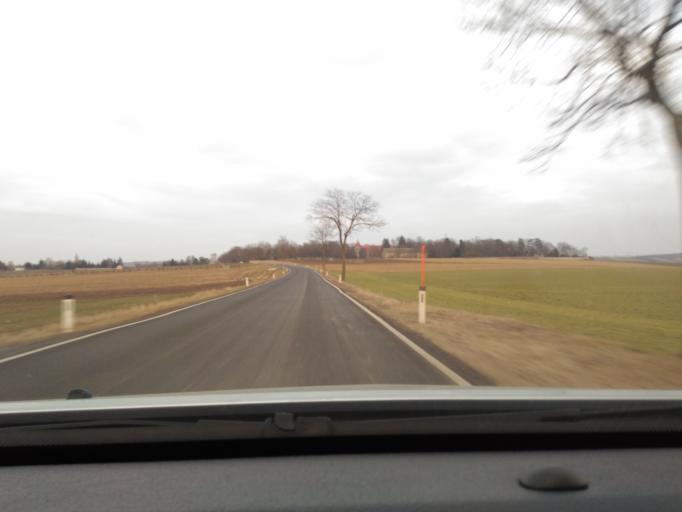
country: AT
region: Lower Austria
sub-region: Politischer Bezirk Mistelbach
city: Drasenhofen
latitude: 48.7465
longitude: 16.6394
